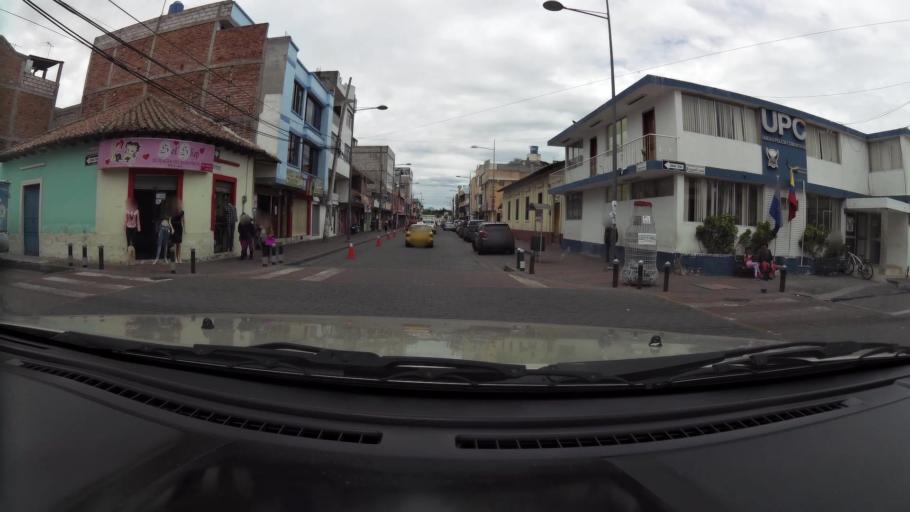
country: EC
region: Cotopaxi
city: San Miguel de Salcedo
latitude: -1.0355
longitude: -78.5903
